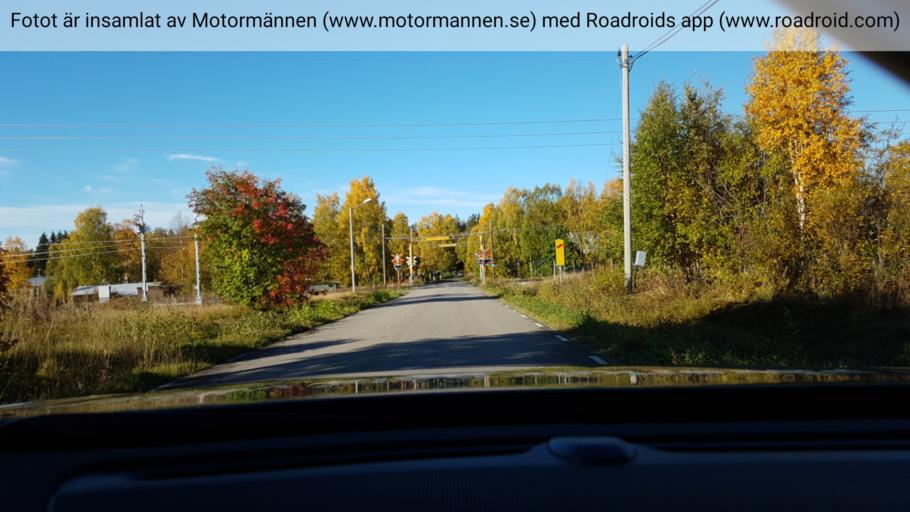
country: SE
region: Norrbotten
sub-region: Alvsbyns Kommun
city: AElvsbyn
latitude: 66.2794
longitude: 21.1257
